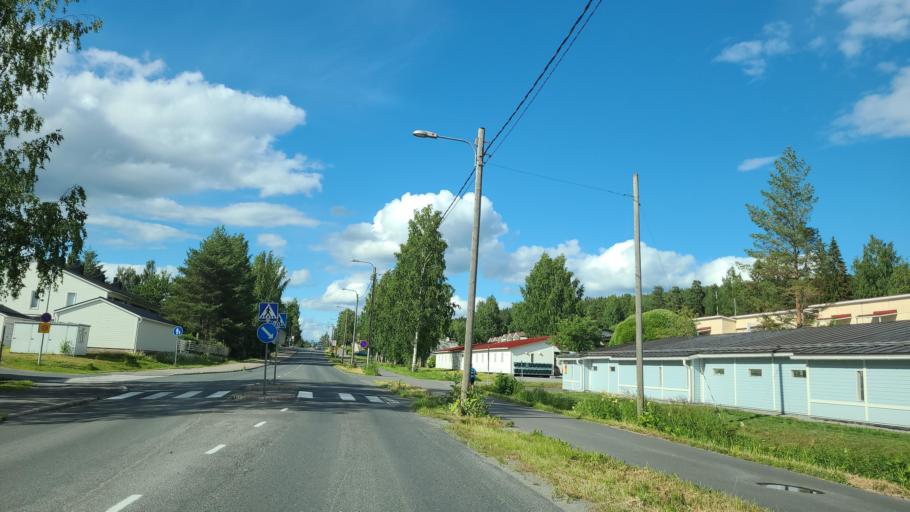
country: FI
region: Northern Savo
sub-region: Kuopio
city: Kuopio
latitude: 62.9231
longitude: 27.6319
